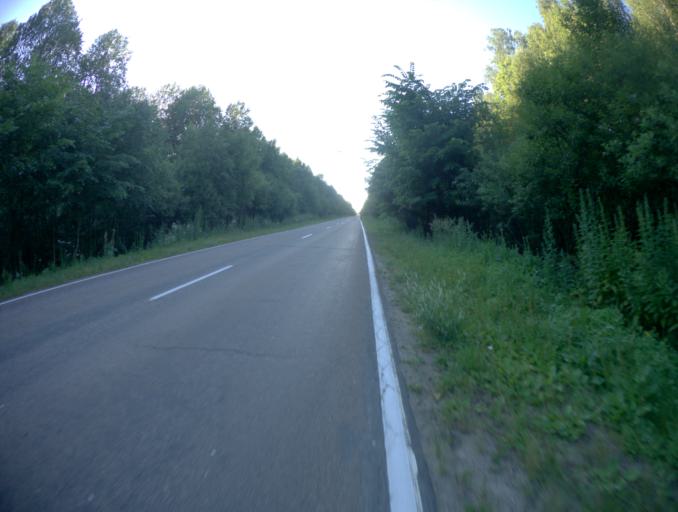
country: RU
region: Vladimir
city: Galitsy
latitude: 56.1401
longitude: 42.8698
